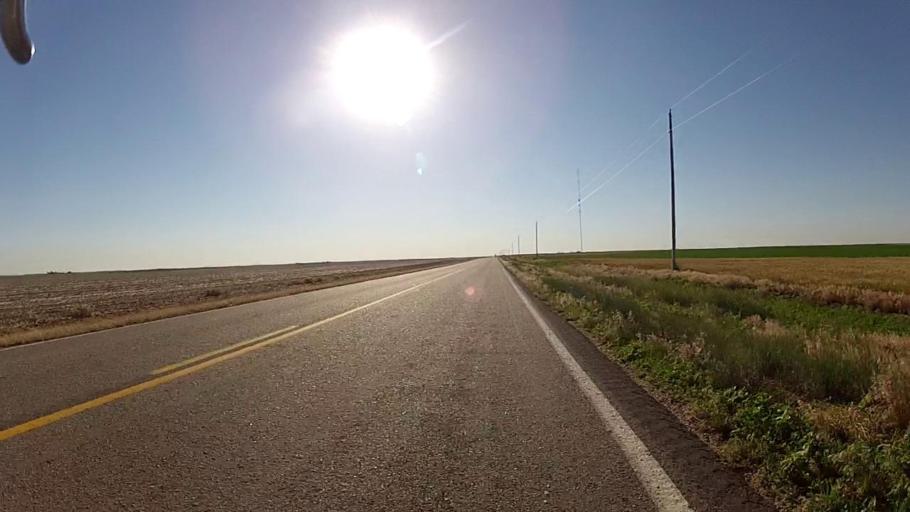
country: US
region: Kansas
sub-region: Ford County
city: Dodge City
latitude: 37.6464
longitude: -99.8488
